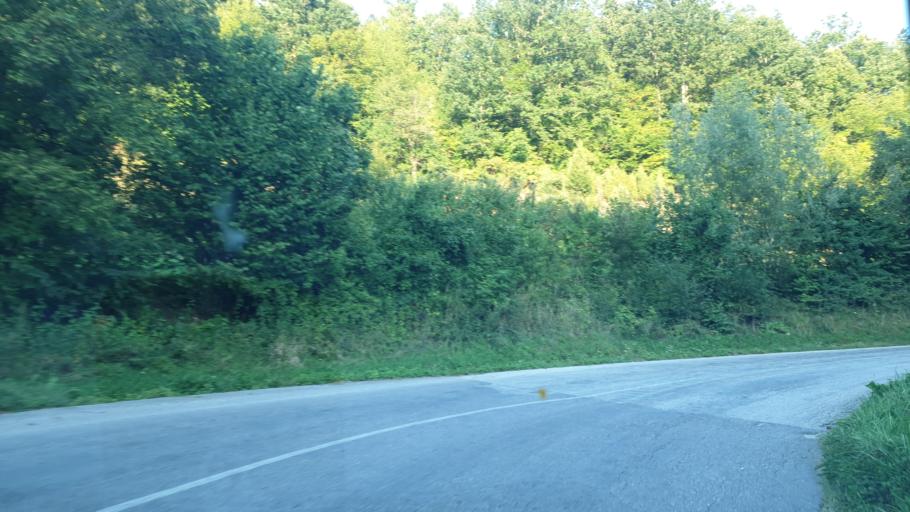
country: RS
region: Central Serbia
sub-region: Zlatiborski Okrug
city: Pozega
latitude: 43.9506
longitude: 20.0241
